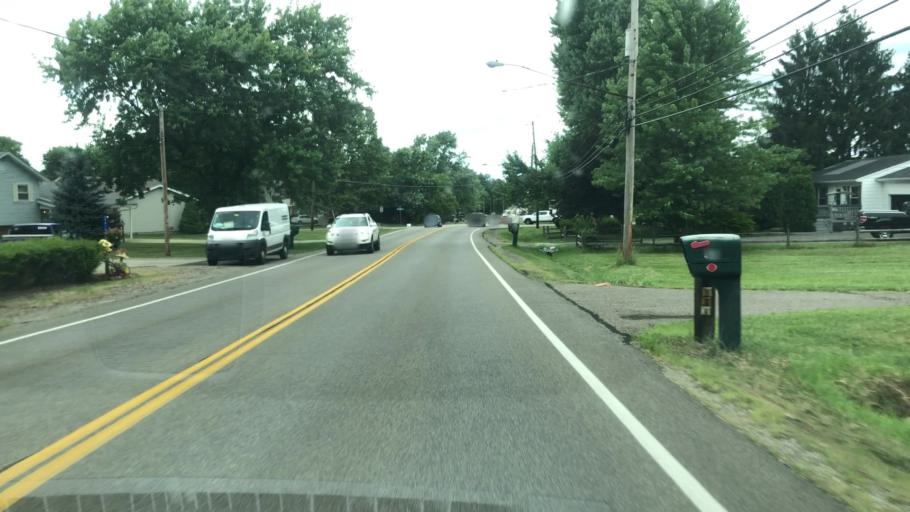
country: US
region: Ohio
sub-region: Summit County
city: Stow
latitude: 41.1782
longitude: -81.4164
